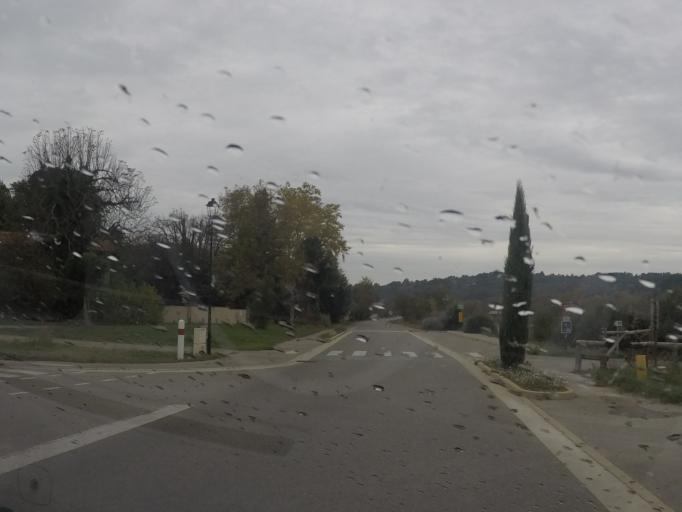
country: FR
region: Provence-Alpes-Cote d'Azur
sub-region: Departement du Vaucluse
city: Goult
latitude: 43.8543
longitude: 5.2743
